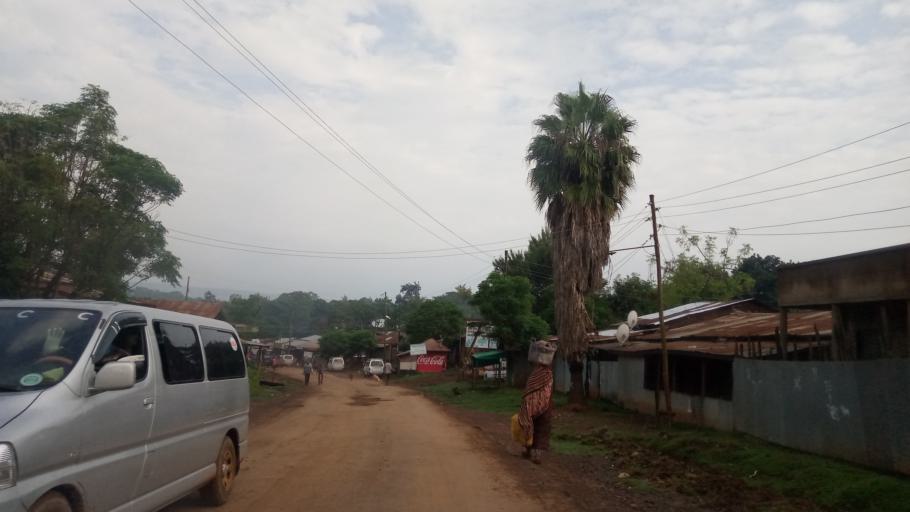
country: ET
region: Oromiya
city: Agaro
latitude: 7.8376
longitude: 36.6704
